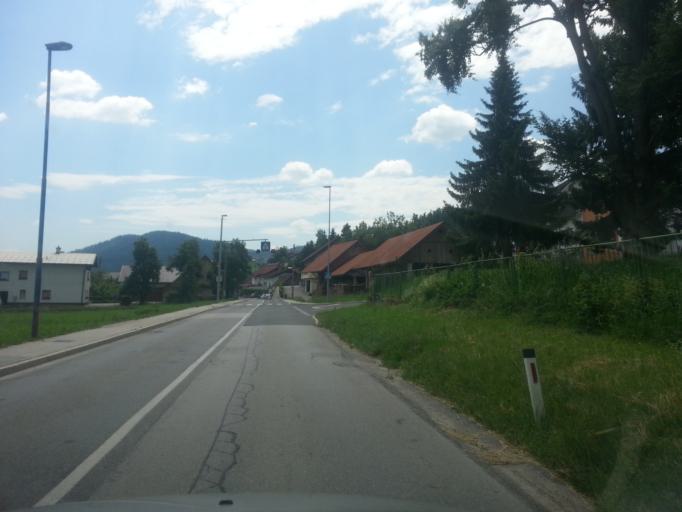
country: SI
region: Vrhnika
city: Vrhnika
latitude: 45.9724
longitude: 14.2930
